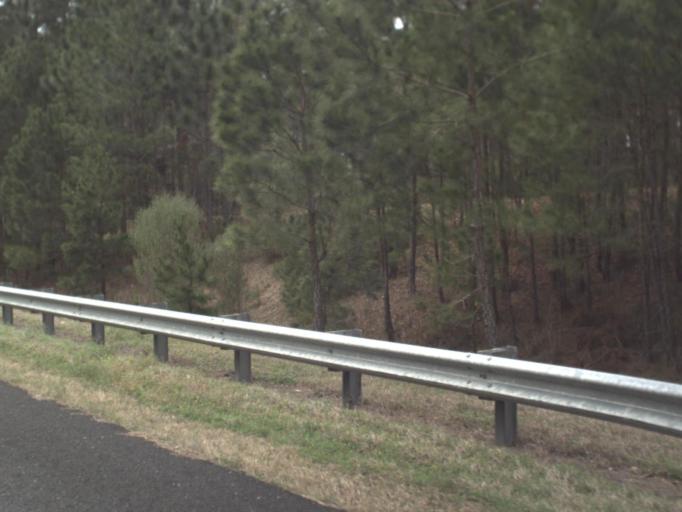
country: US
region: Georgia
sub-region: Grady County
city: Cairo
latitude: 30.6711
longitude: -84.1614
